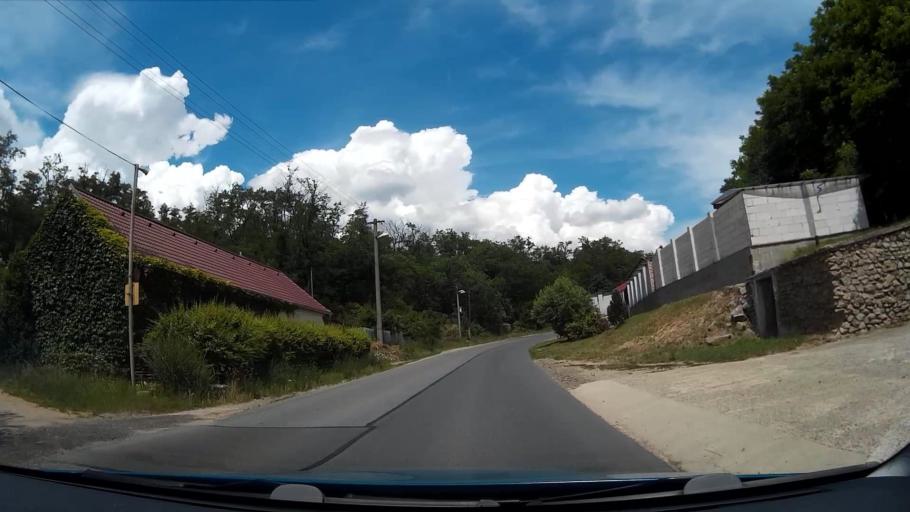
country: CZ
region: South Moravian
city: Dolni Kounice
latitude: 49.0519
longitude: 16.5020
